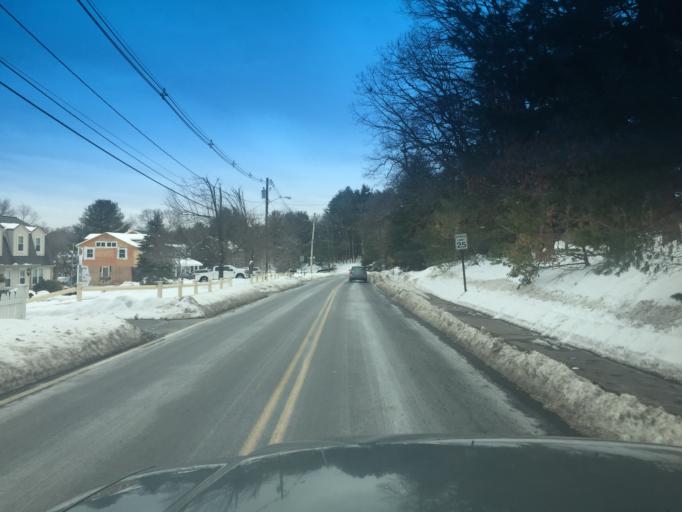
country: US
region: Massachusetts
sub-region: Norfolk County
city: Norfolk
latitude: 42.1047
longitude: -71.2822
